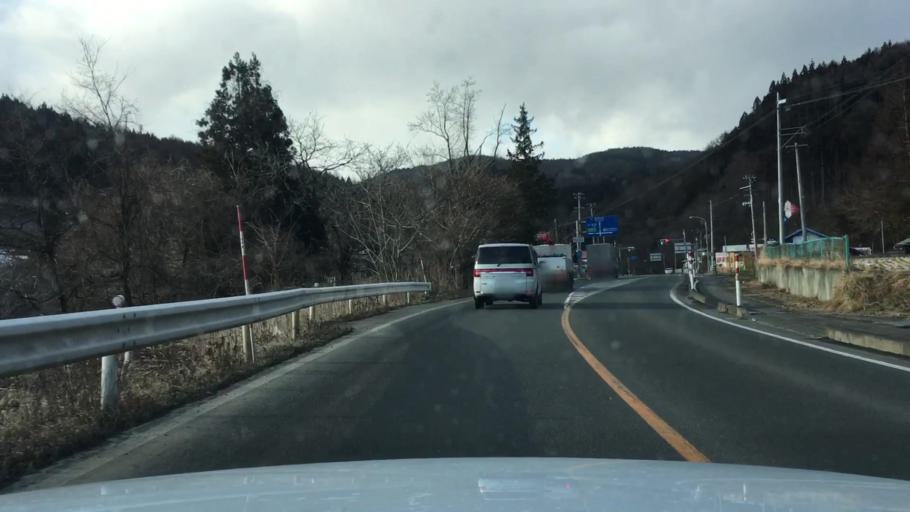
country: JP
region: Iwate
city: Morioka-shi
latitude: 39.6733
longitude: 141.2115
